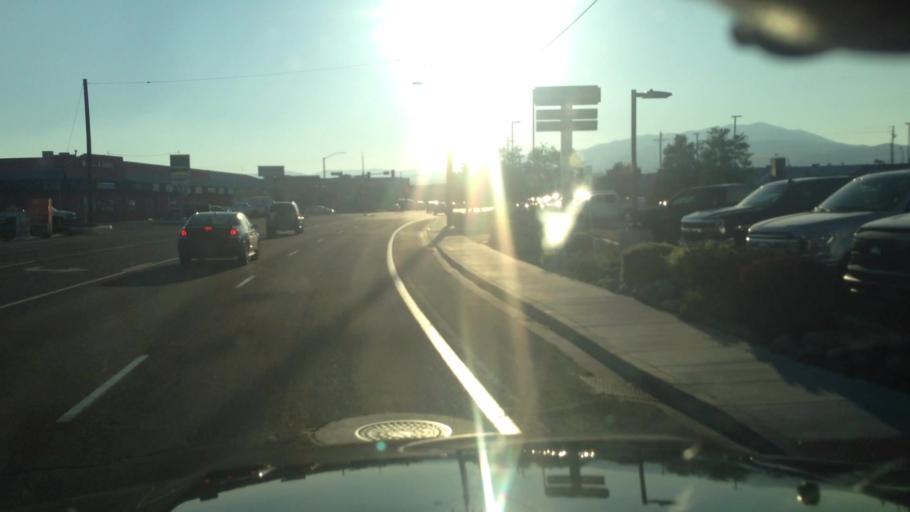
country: US
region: Nevada
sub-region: Washoe County
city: Sparks
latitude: 39.5172
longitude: -119.7754
